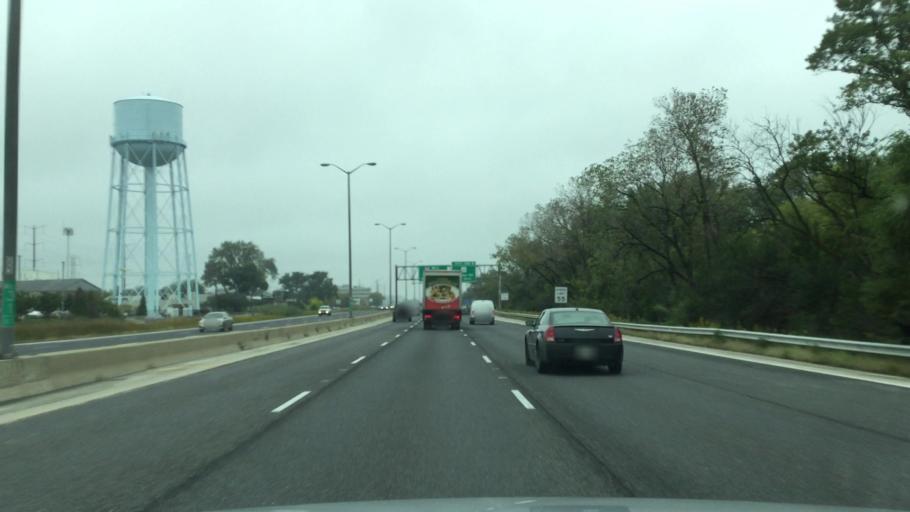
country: US
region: Illinois
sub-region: Cook County
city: Northfield
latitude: 42.1182
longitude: -87.7788
